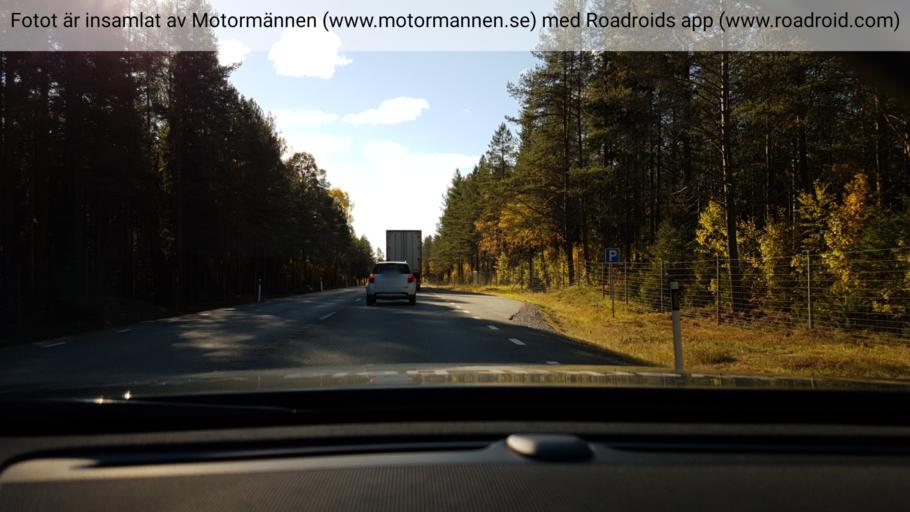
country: SE
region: Vaesterbotten
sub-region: Skelleftea Kommun
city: Burea
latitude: 64.5271
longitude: 21.2581
